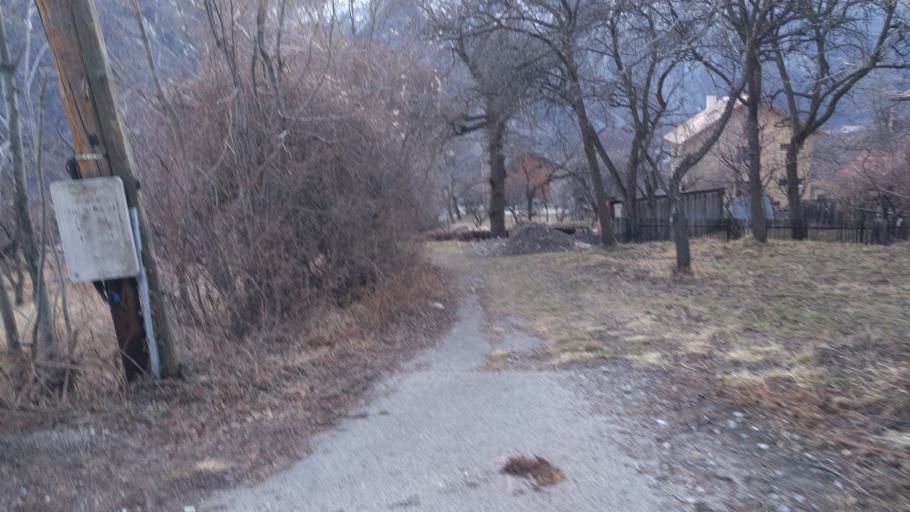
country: FR
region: Rhone-Alpes
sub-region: Departement de la Savoie
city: Villargondran
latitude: 45.2548
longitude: 6.4198
